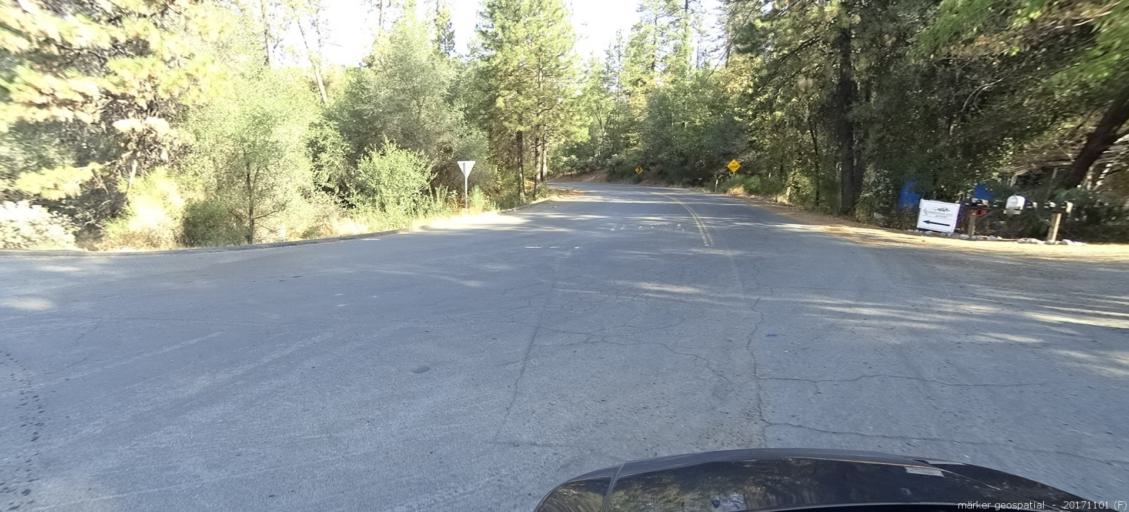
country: US
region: California
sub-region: Shasta County
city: Shasta Lake
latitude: 40.7305
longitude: -122.3184
